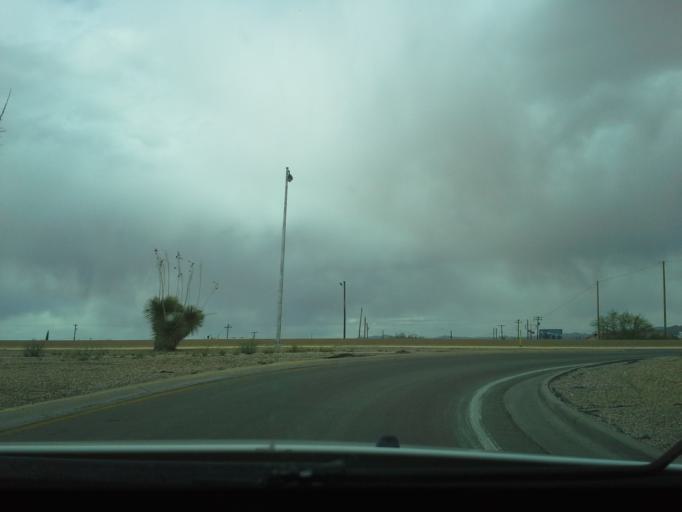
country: US
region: New Mexico
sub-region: Hidalgo County
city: Lordsburg
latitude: 32.3502
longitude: -108.7106
